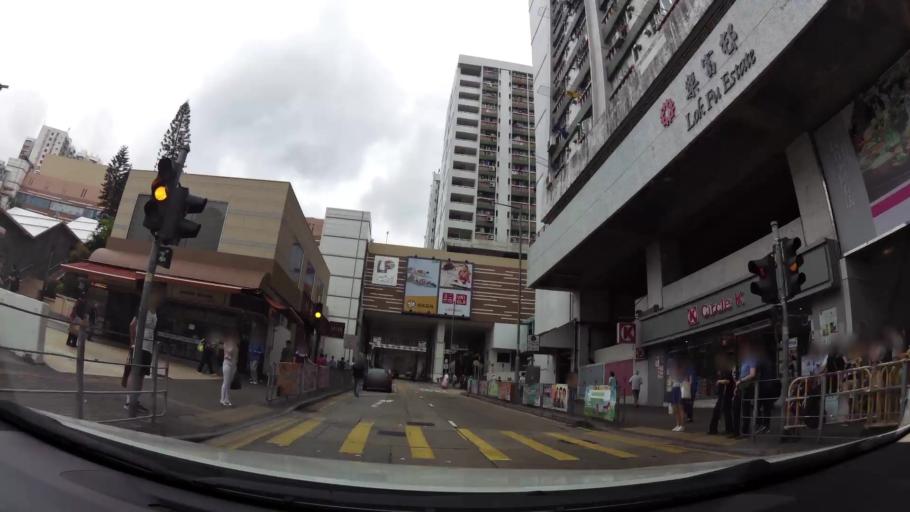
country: HK
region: Wong Tai Sin
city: Wong Tai Sin
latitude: 22.3386
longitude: 114.1879
